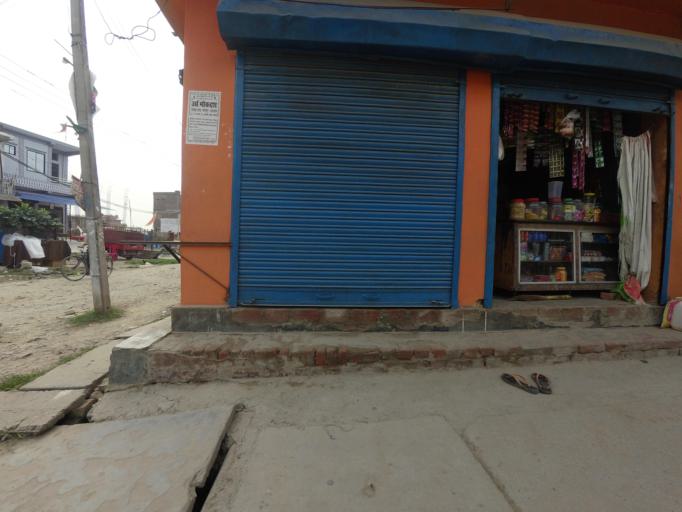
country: NP
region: Western Region
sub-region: Lumbini Zone
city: Bhairahawa
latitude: 27.4982
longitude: 83.4506
